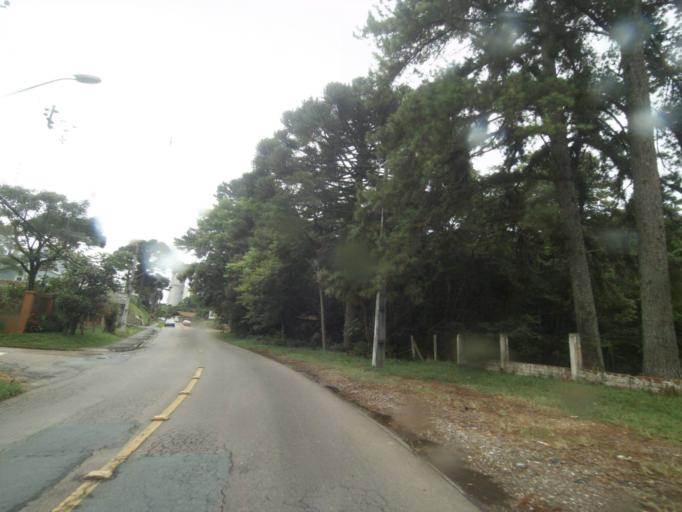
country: BR
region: Parana
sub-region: Curitiba
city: Curitiba
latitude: -25.4478
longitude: -49.3348
